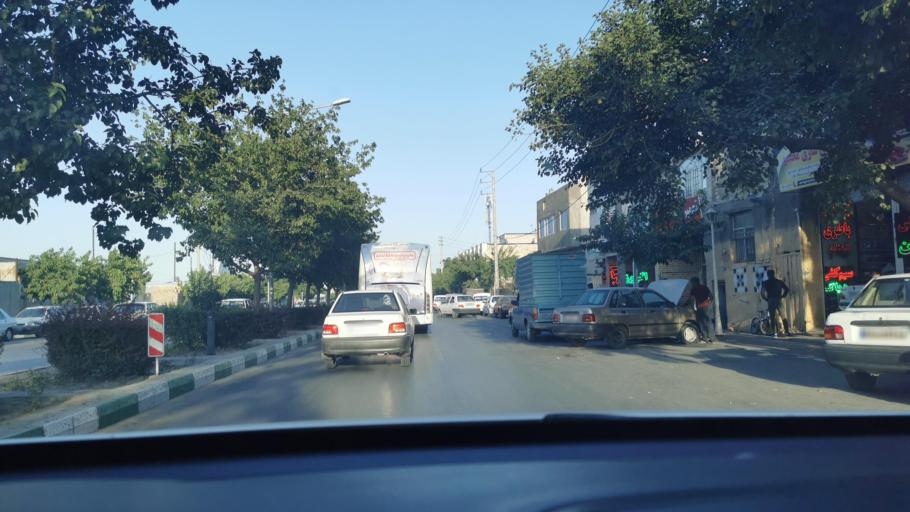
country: IR
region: Razavi Khorasan
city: Mashhad
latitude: 36.2896
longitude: 59.6519
